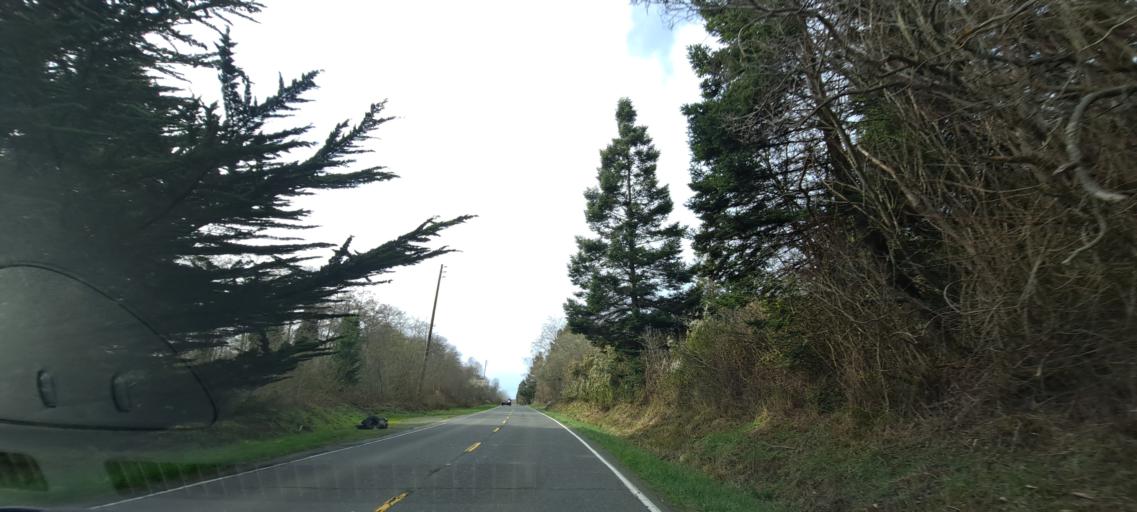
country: US
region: California
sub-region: Humboldt County
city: Fortuna
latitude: 40.6133
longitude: -124.1935
